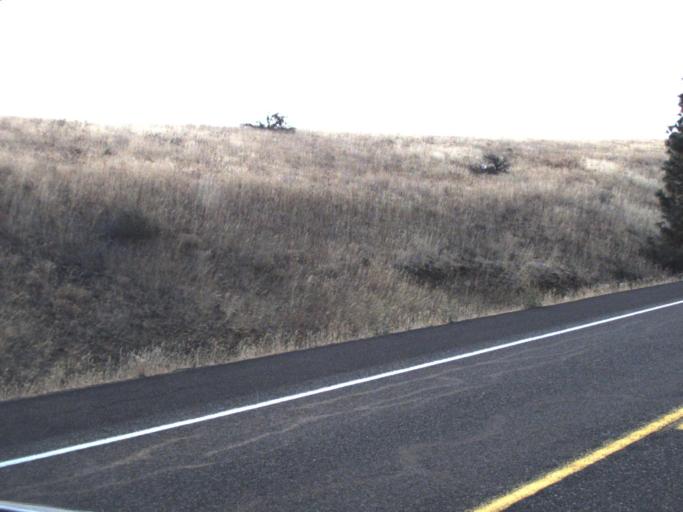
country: US
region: Washington
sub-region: Kittitas County
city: Ellensburg
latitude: 47.1553
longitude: -120.6995
